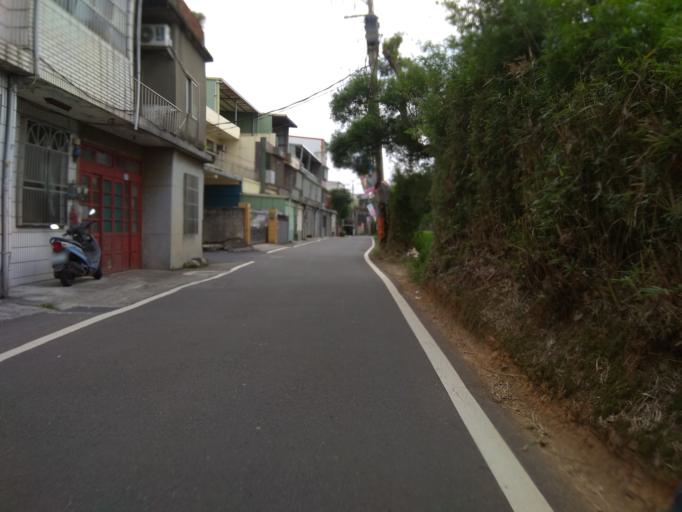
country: TW
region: Taiwan
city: Daxi
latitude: 24.9321
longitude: 121.2048
